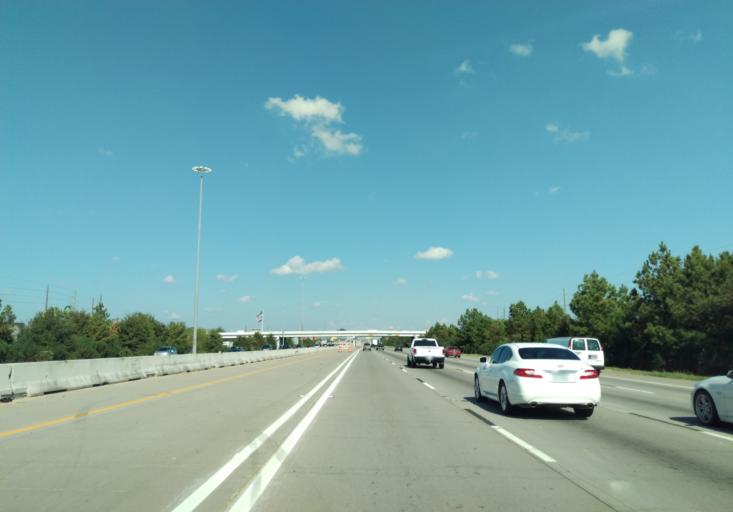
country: US
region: Texas
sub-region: Harris County
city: Spring
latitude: 30.0639
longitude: -95.4339
